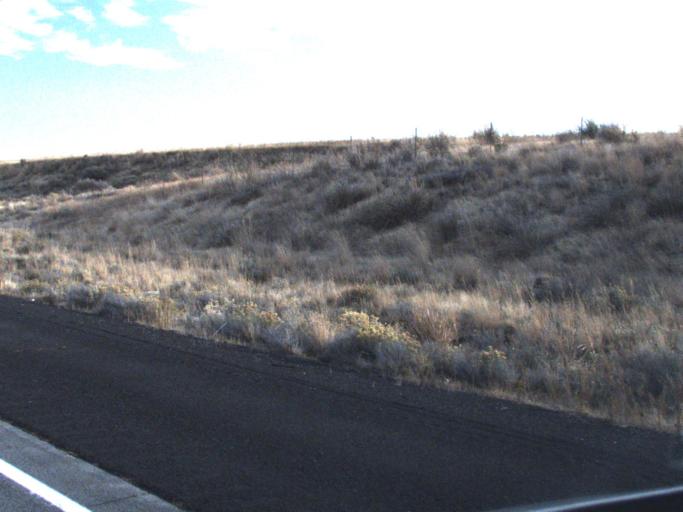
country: US
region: Washington
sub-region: Adams County
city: Ritzville
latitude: 46.9483
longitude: -118.5782
